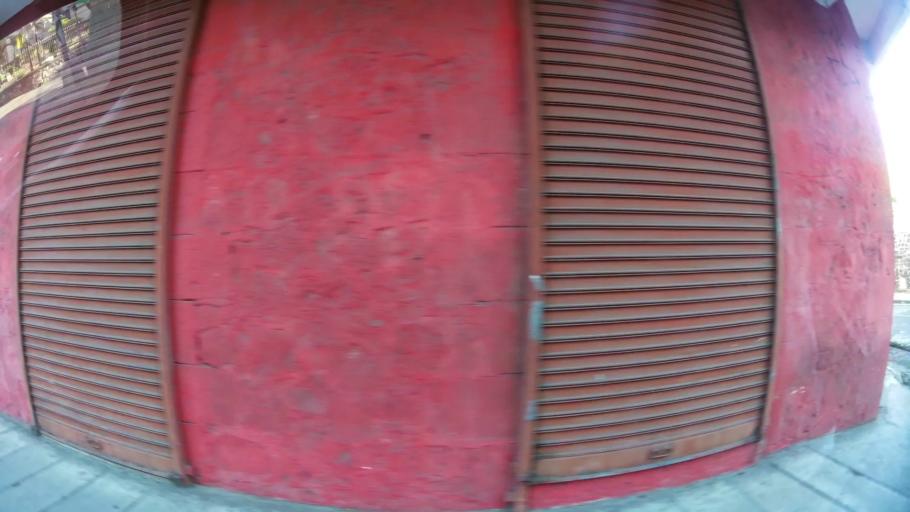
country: MU
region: Port Louis
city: Port Louis
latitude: -20.1684
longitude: 57.5057
